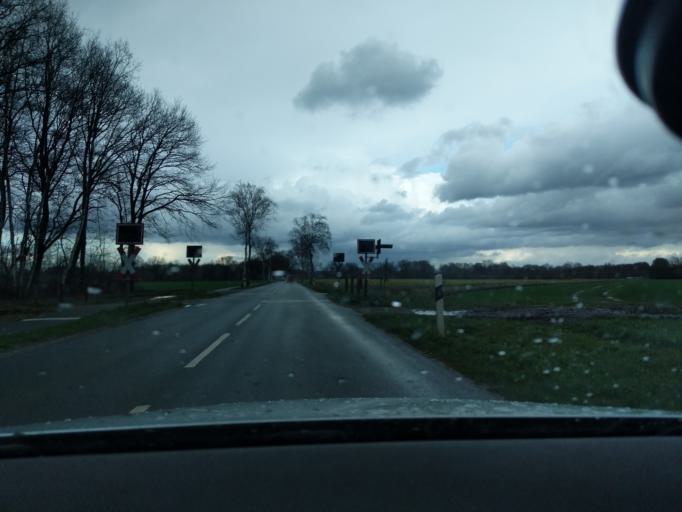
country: DE
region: Lower Saxony
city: Kutenholz
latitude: 53.5131
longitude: 9.3693
